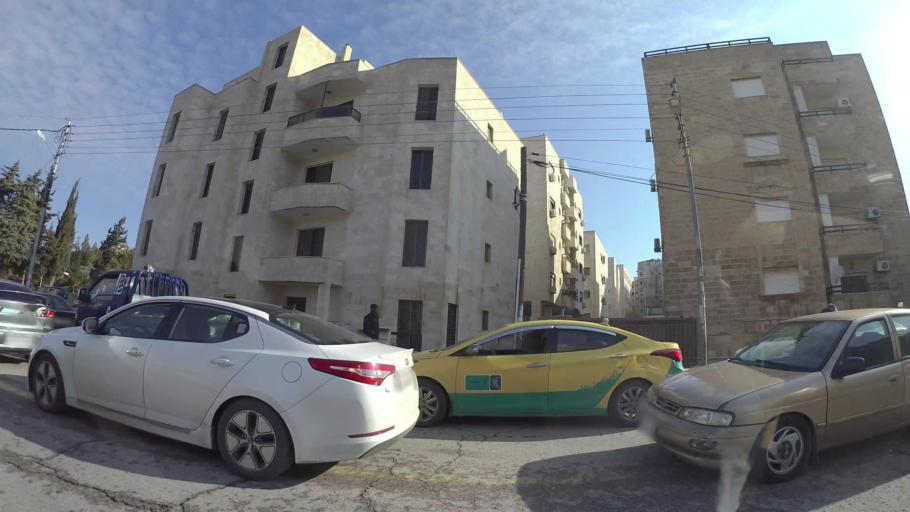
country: JO
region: Amman
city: Al Jubayhah
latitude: 32.0057
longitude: 35.8794
